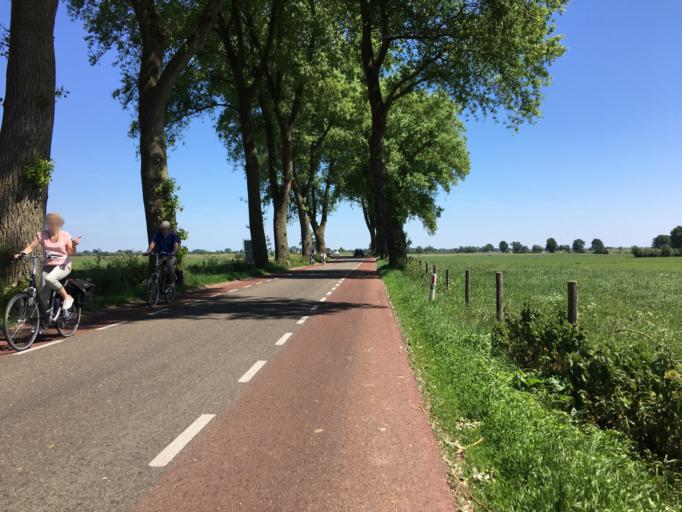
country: NL
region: Gelderland
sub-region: Gemeente Zaltbommel
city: Nederhemert-Noord
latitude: 51.7468
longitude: 5.1652
